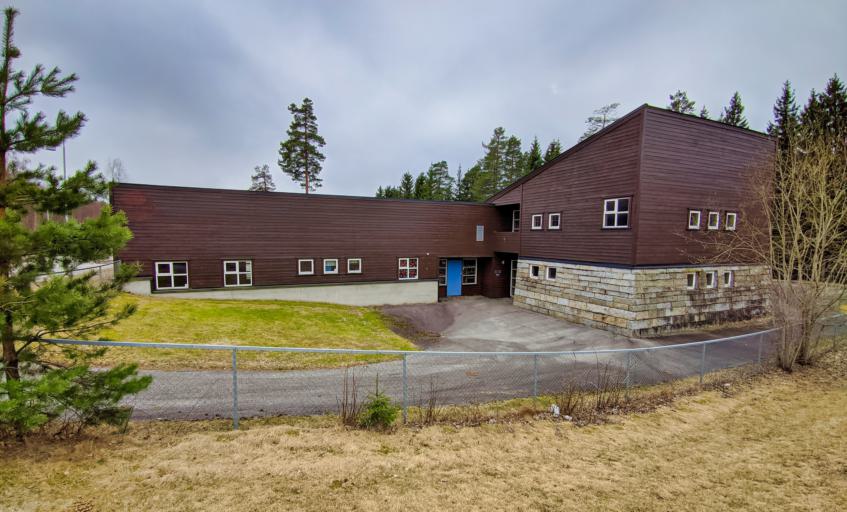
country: NO
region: Akershus
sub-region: Ullensaker
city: Jessheim
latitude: 60.1658
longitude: 11.1458
